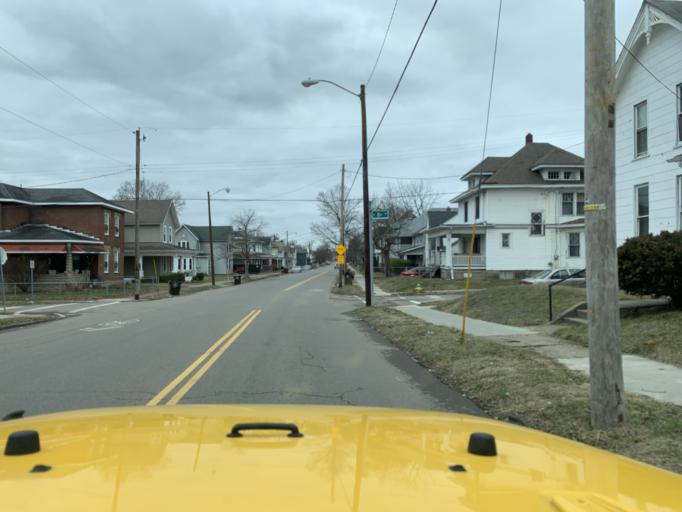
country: US
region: Ohio
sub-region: Licking County
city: Newark
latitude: 40.0570
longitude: -82.4115
